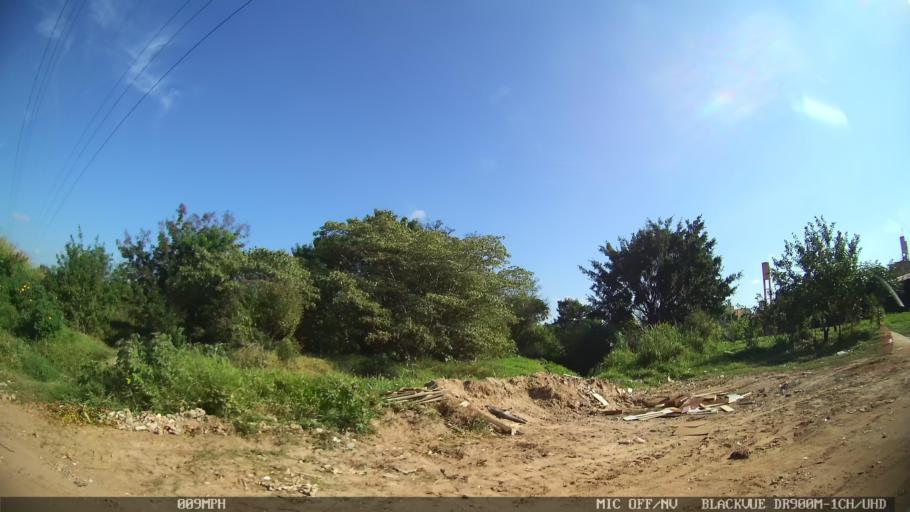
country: BR
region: Sao Paulo
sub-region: Campinas
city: Campinas
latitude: -22.9527
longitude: -47.1210
